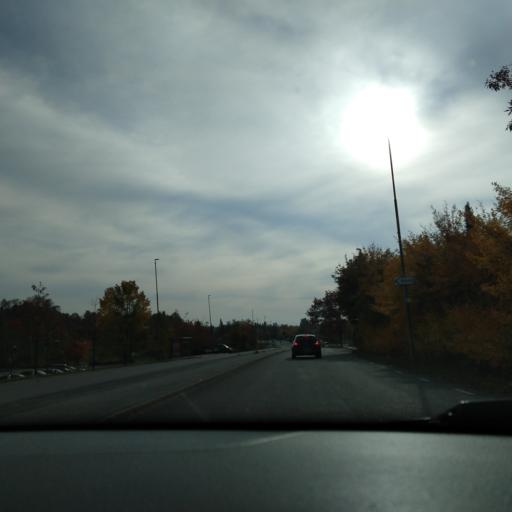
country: SE
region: Stockholm
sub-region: Upplands Vasby Kommun
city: Upplands Vaesby
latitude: 59.5161
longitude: 17.9186
